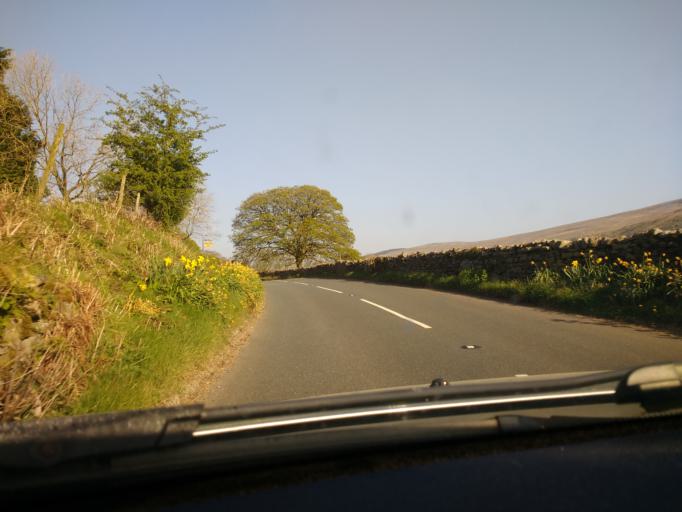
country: GB
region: England
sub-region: Cumbria
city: Sedbergh
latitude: 54.3106
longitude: -2.4306
